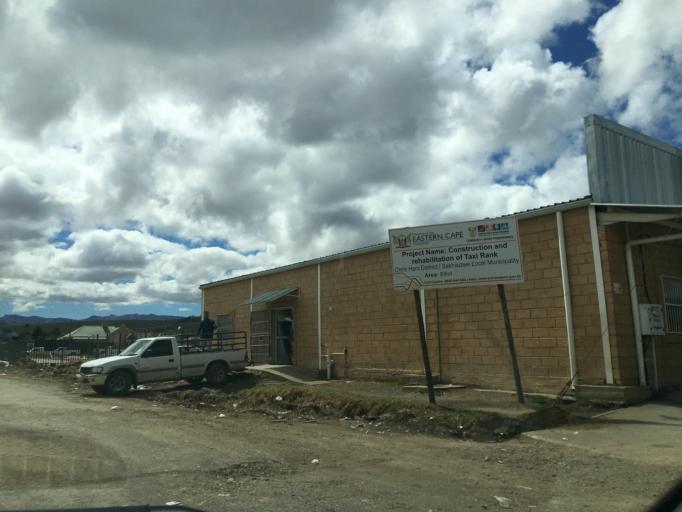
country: ZA
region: Eastern Cape
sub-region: Chris Hani District Municipality
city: Elliot
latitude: -31.3351
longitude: 27.8461
